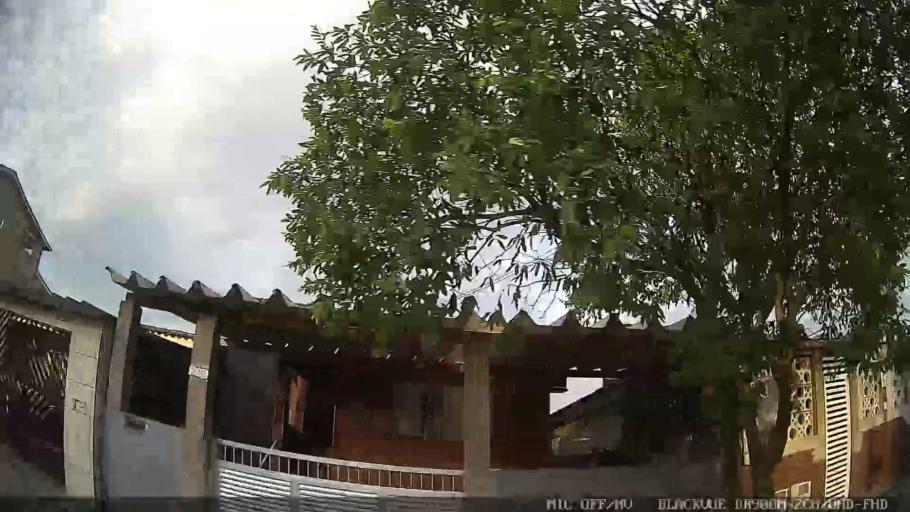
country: BR
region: Sao Paulo
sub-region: Cubatao
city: Cubatao
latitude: -23.8941
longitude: -46.4275
